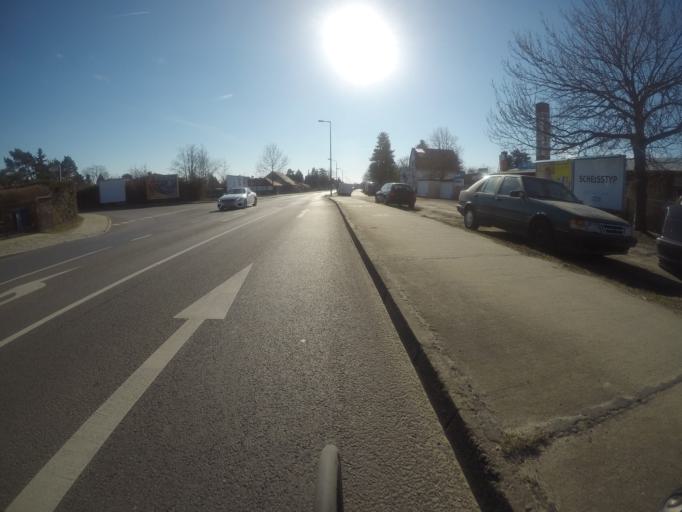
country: DE
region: Berlin
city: Kaulsdorf
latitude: 52.5034
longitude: 13.5809
